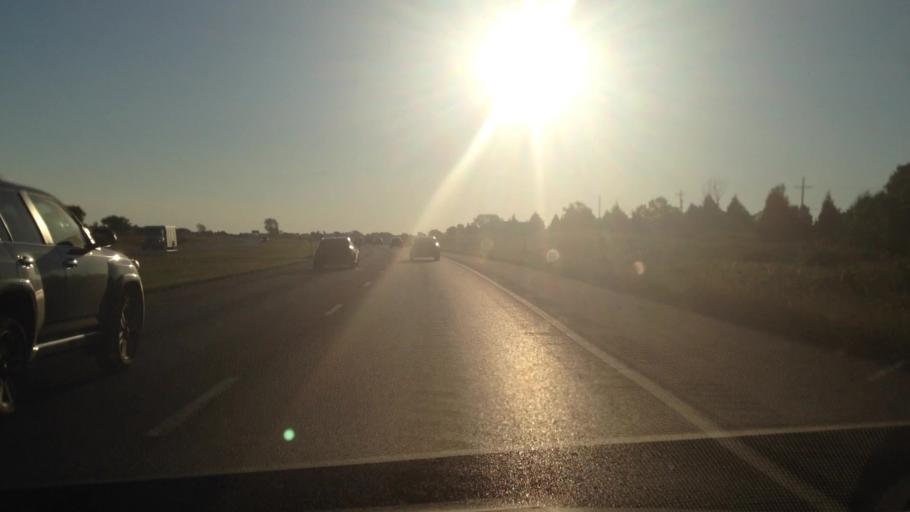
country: US
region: Kansas
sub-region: Douglas County
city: Eudora
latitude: 38.9418
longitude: -95.0456
